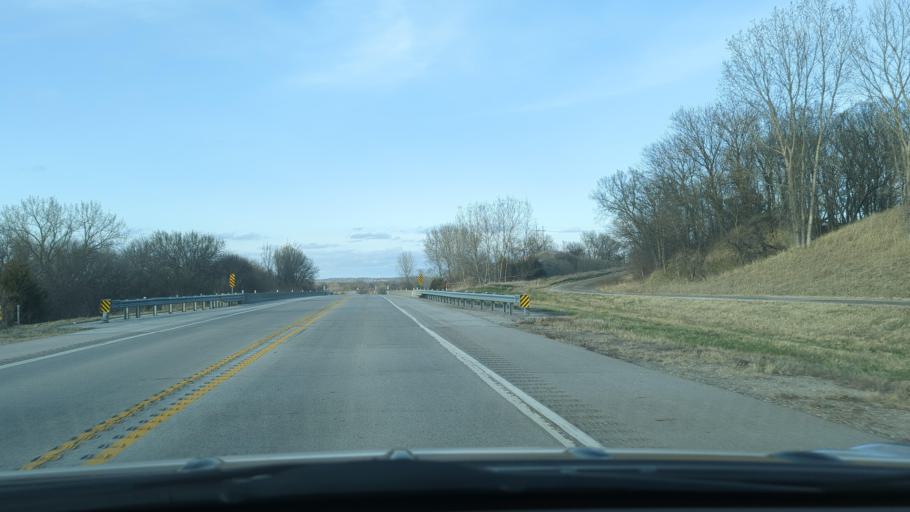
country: US
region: Nebraska
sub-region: Saunders County
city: Ashland
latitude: 41.0482
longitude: -96.3426
